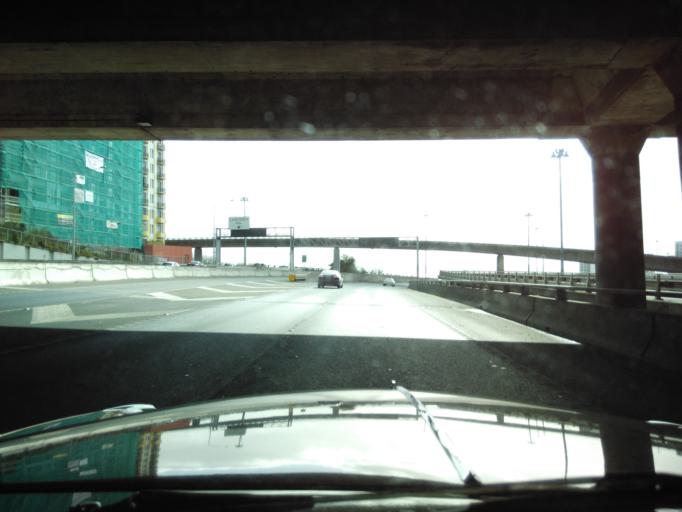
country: NZ
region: Auckland
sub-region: Auckland
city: Auckland
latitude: -36.8584
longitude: 174.7562
